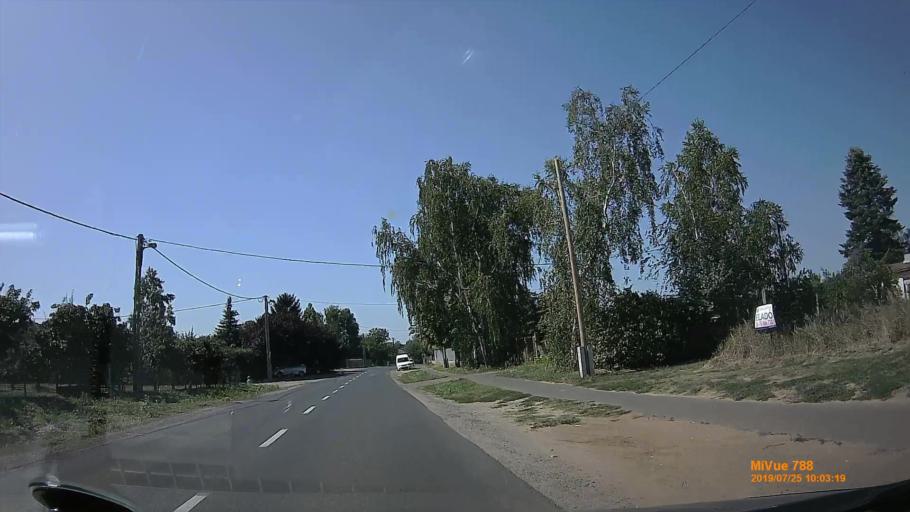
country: HU
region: Szabolcs-Szatmar-Bereg
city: Kotaj
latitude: 48.0231
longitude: 21.7445
